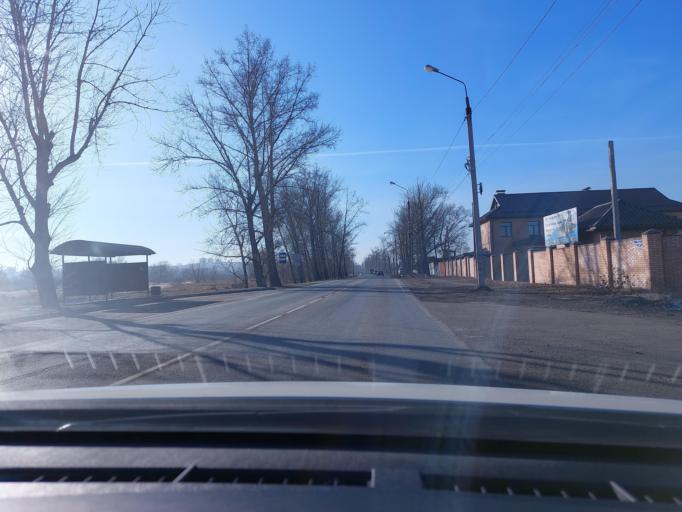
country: RU
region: Irkutsk
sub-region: Irkutskiy Rayon
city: Irkutsk
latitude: 52.3066
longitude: 104.2557
